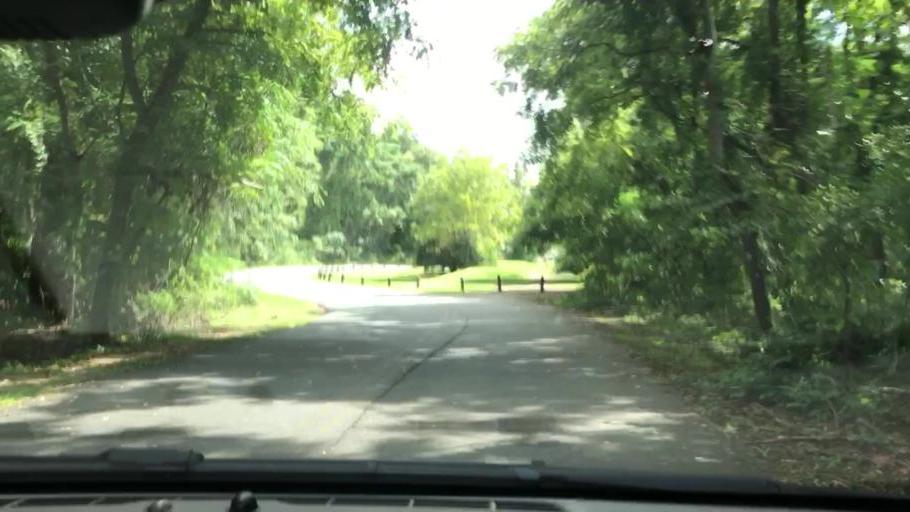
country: US
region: Georgia
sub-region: Stewart County
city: Lumpkin
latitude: 32.0710
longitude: -84.9130
